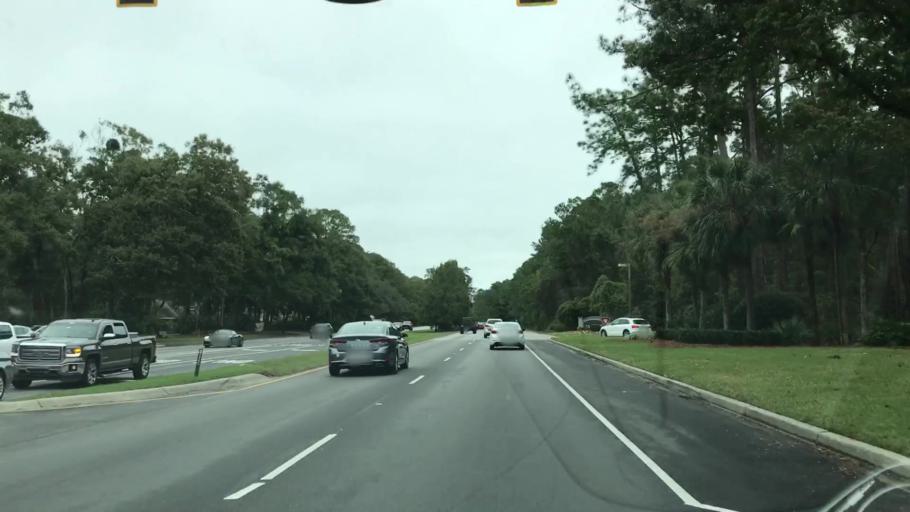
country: US
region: South Carolina
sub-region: Beaufort County
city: Hilton Head Island
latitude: 32.2150
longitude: -80.7203
